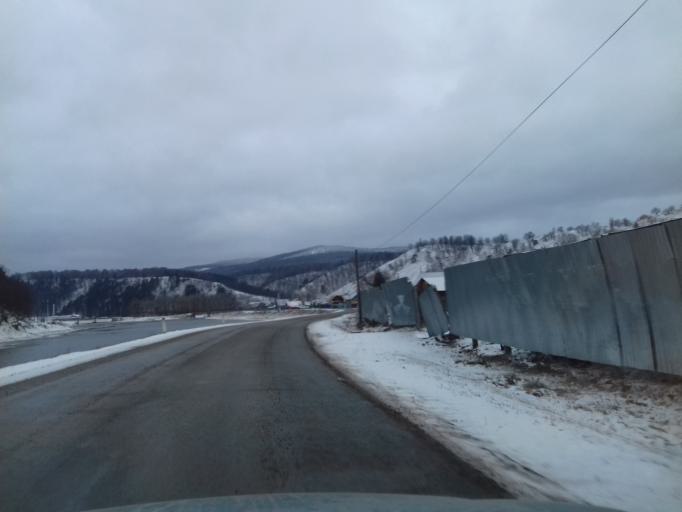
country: RU
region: Bashkortostan
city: Starosubkhangulovo
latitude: 53.0961
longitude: 57.4407
